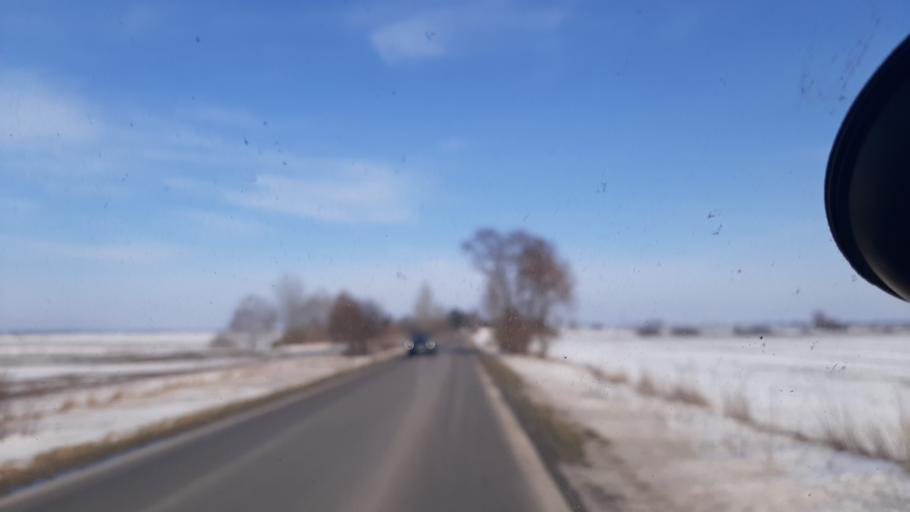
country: PL
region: Lublin Voivodeship
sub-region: Powiat pulawski
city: Kurow
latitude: 51.3724
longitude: 22.1506
